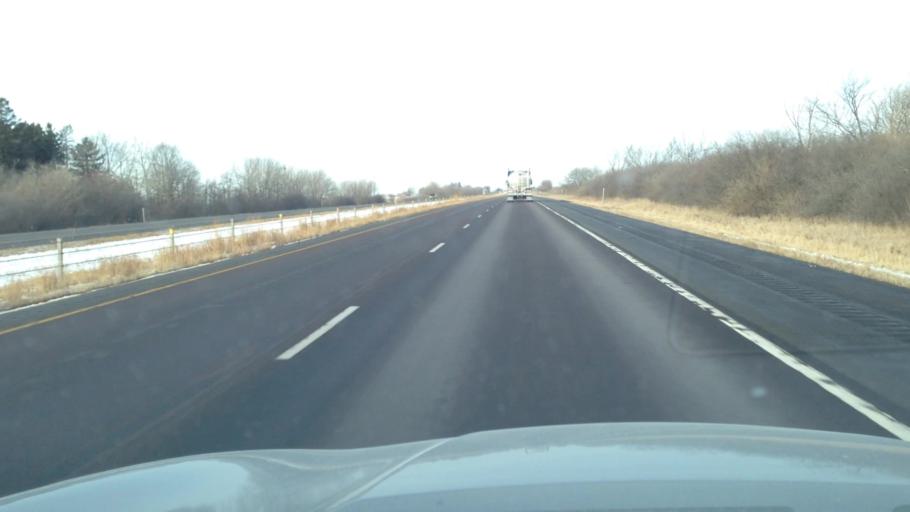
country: US
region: Iowa
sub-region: Poweshiek County
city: Grinnell
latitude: 41.6959
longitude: -92.6054
